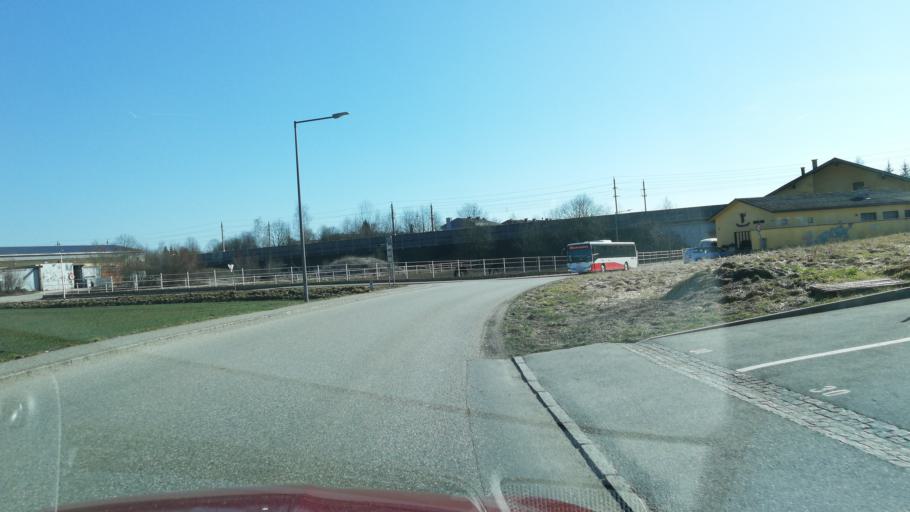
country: AT
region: Upper Austria
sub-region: Politischer Bezirk Vocklabruck
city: Schwanenstadt
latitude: 48.0616
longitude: 13.7767
